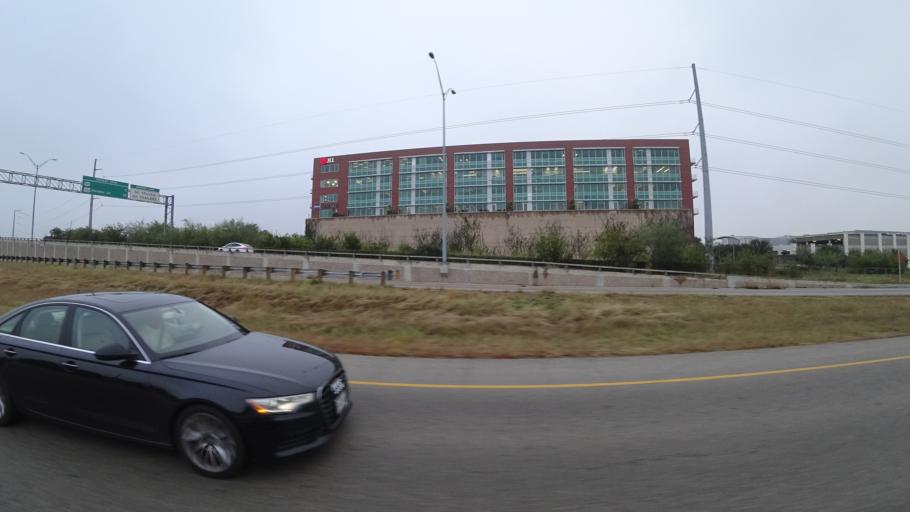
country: US
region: Texas
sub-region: Travis County
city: Austin
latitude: 30.2745
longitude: -97.7665
